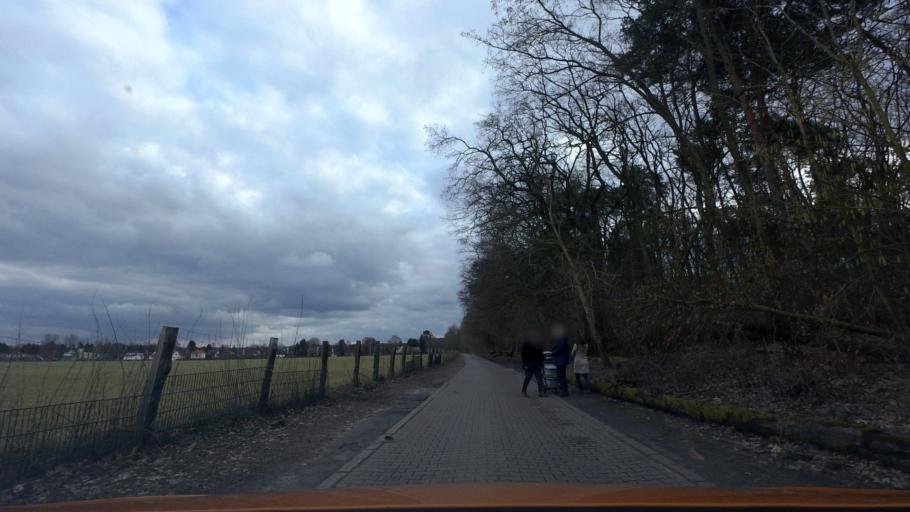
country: DE
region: Berlin
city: Konradshohe
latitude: 52.6001
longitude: 13.2298
